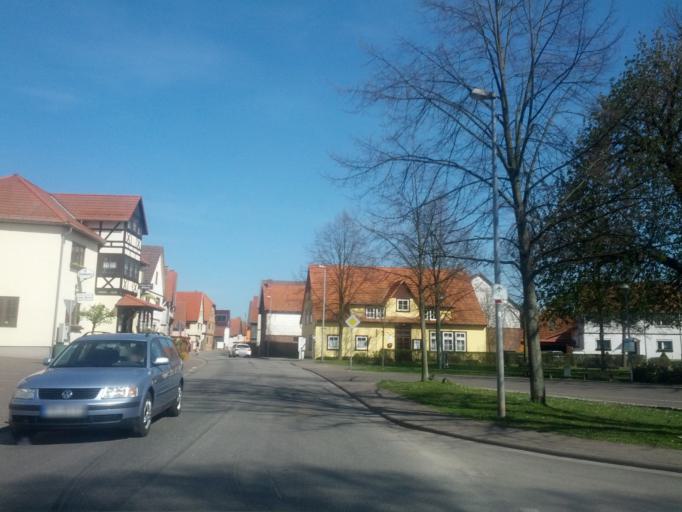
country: DE
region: Thuringia
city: Mechterstadt
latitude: 50.9418
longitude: 10.5228
